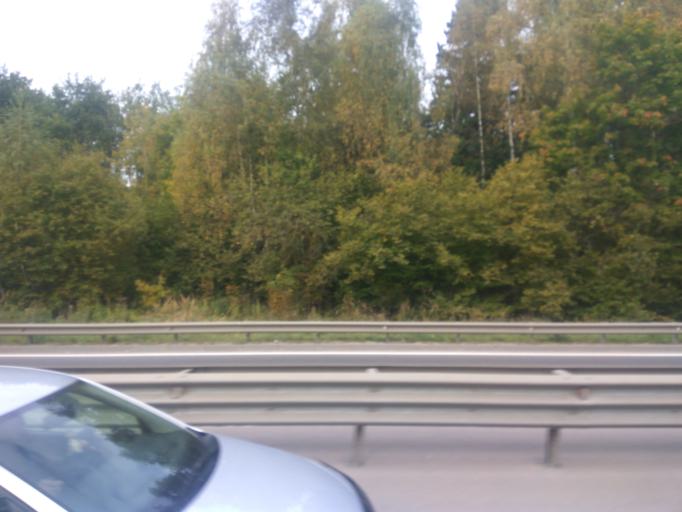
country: RU
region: Moskovskaya
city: Fryazino
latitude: 55.9423
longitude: 38.0367
